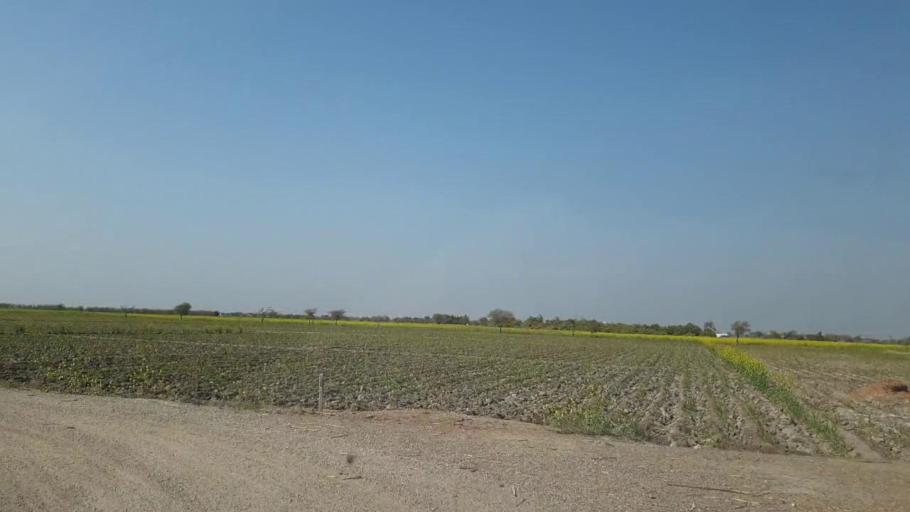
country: PK
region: Sindh
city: Mirpur Khas
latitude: 25.7359
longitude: 69.1614
